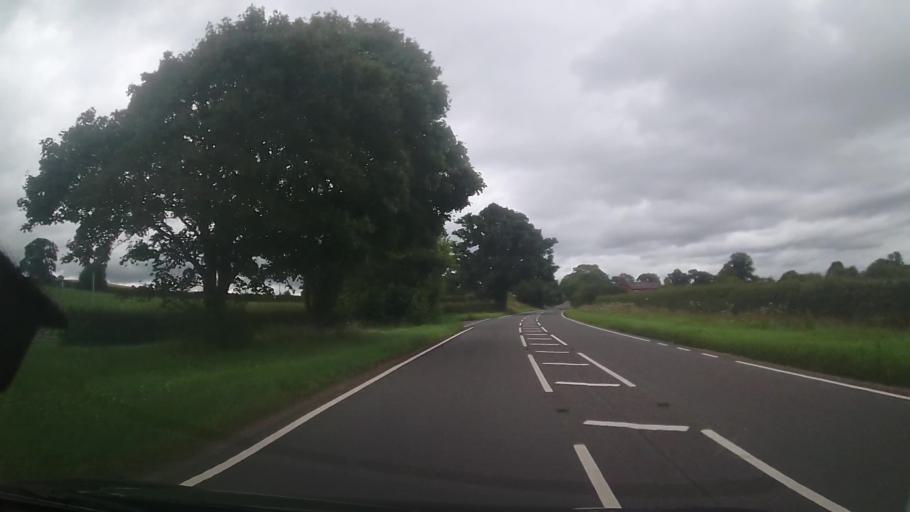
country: GB
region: England
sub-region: Shropshire
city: Ellesmere
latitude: 52.9165
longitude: -2.8326
